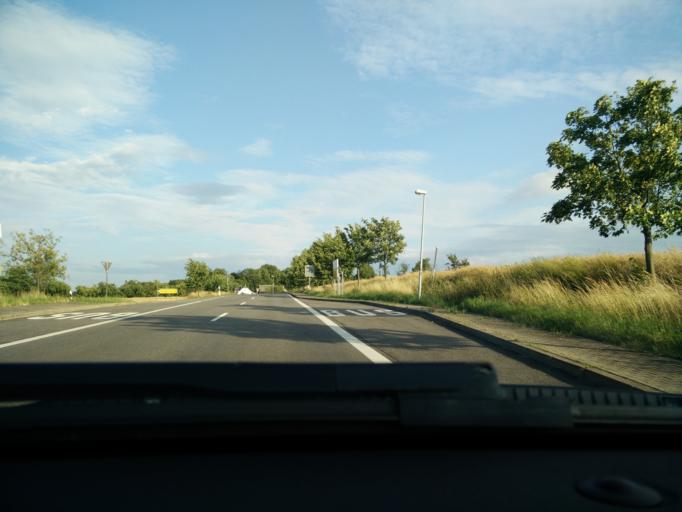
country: DE
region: Saxony
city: Geithain
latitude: 51.0866
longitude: 12.7120
